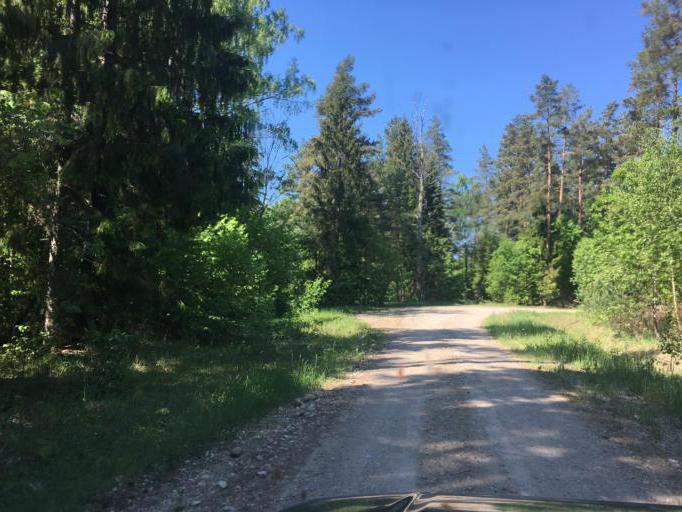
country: LV
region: Talsu Rajons
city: Valdemarpils
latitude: 57.4469
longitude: 22.6554
